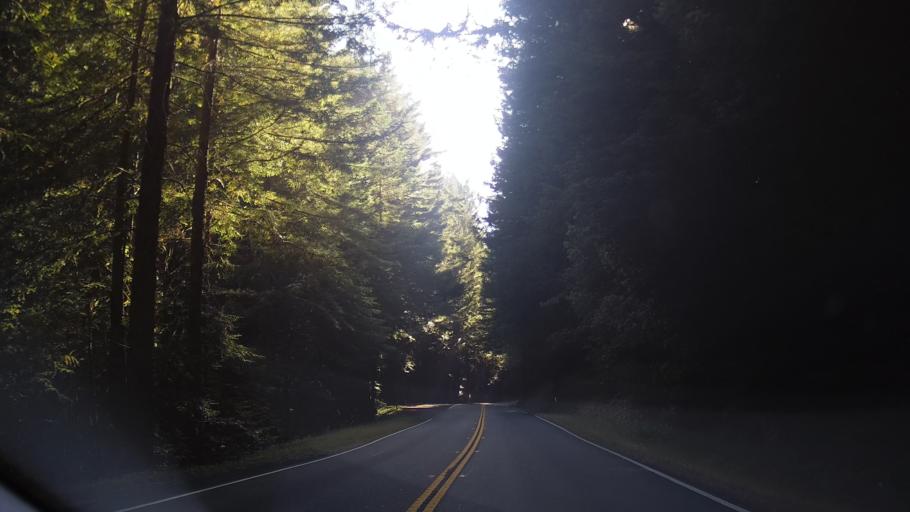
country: US
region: California
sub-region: Mendocino County
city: Brooktrails
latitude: 39.3489
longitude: -123.5786
